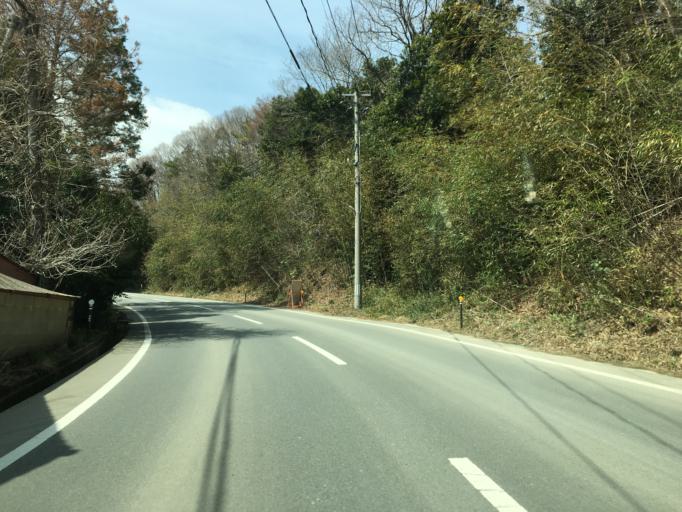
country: JP
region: Fukushima
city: Namie
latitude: 37.4548
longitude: 140.9762
